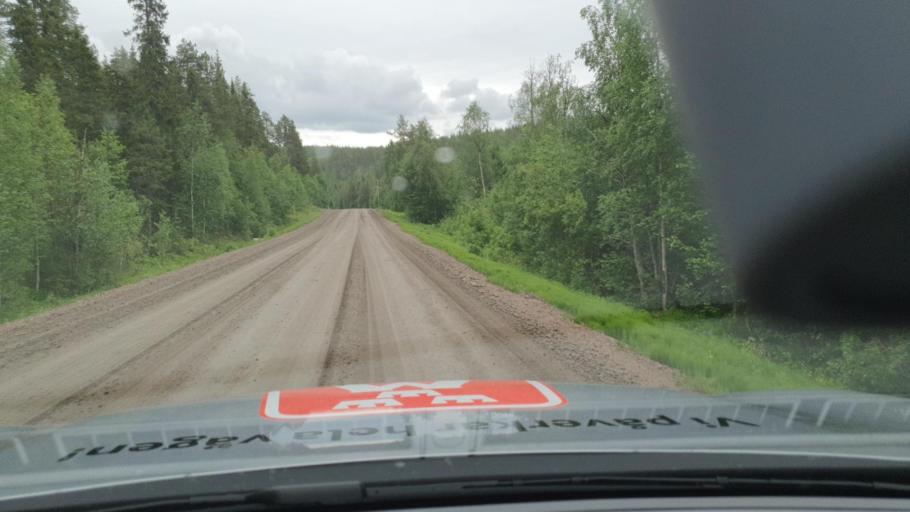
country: SE
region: Norrbotten
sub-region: Overtornea Kommun
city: OEvertornea
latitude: 66.4248
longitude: 23.5408
